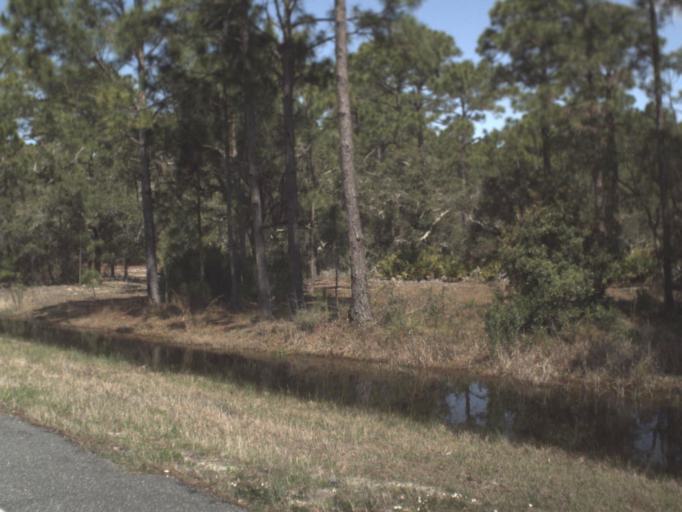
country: US
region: Florida
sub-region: Wakulla County
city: Crawfordville
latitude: 29.9902
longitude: -84.3920
